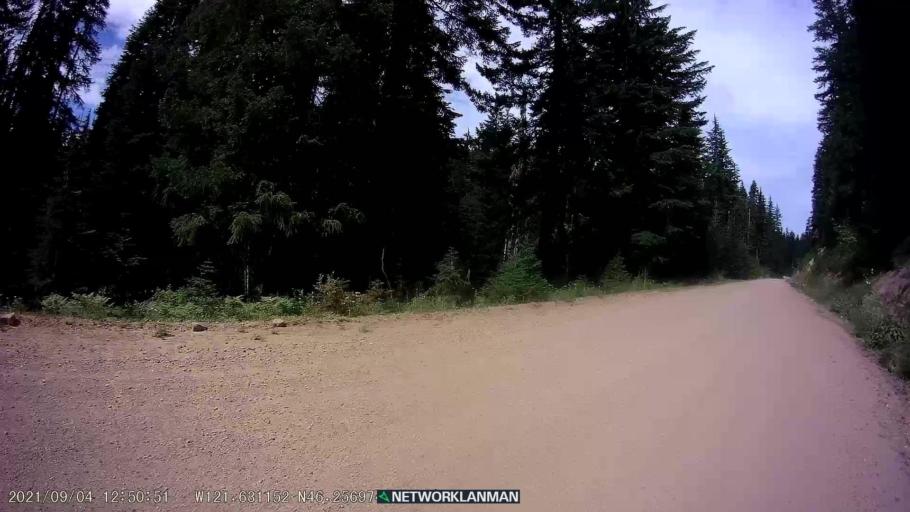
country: US
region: Washington
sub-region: Klickitat County
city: White Salmon
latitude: 46.2571
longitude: -121.6311
